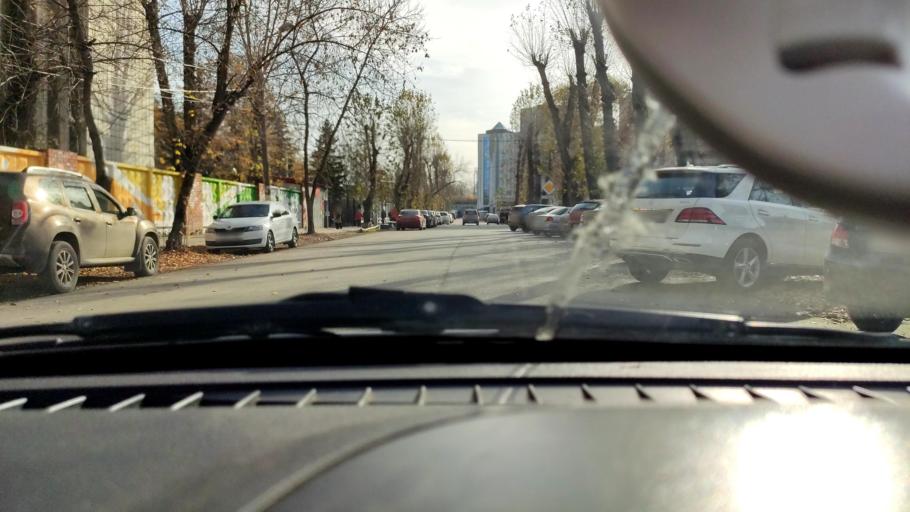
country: RU
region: Perm
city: Perm
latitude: 58.0076
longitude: 56.1835
